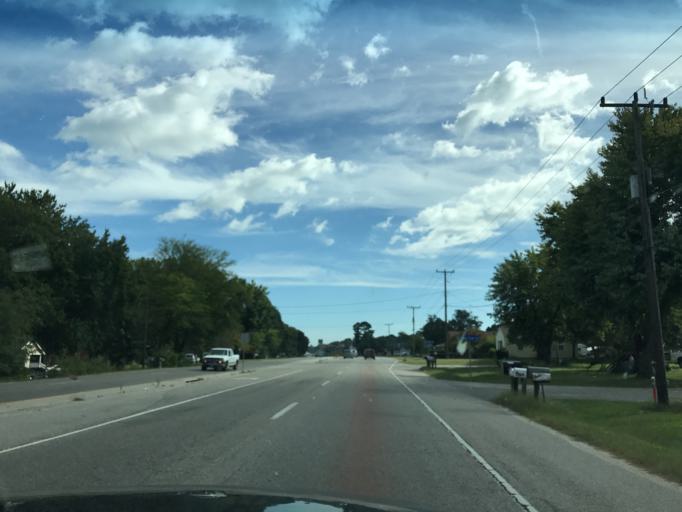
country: US
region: Virginia
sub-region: Gloucester County
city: Gloucester Point
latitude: 37.2998
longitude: -76.5120
